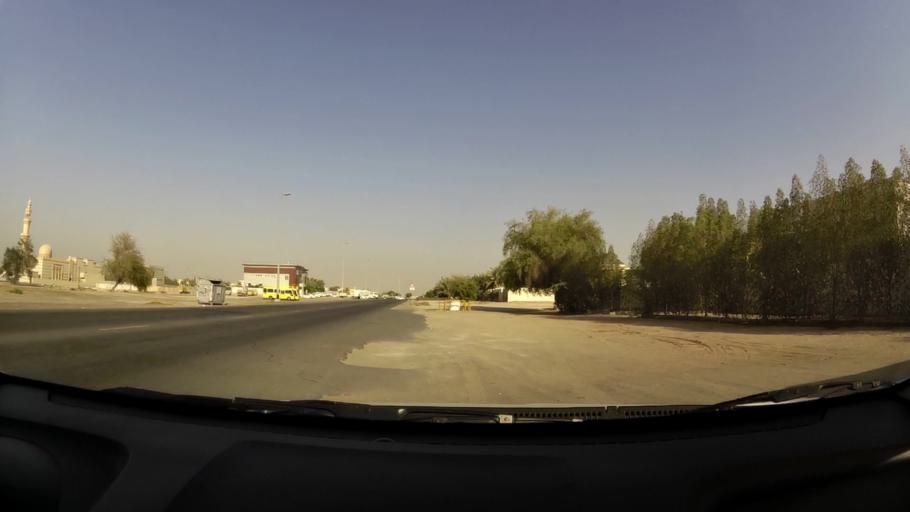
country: AE
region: Ash Shariqah
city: Sharjah
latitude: 25.2702
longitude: 55.3855
